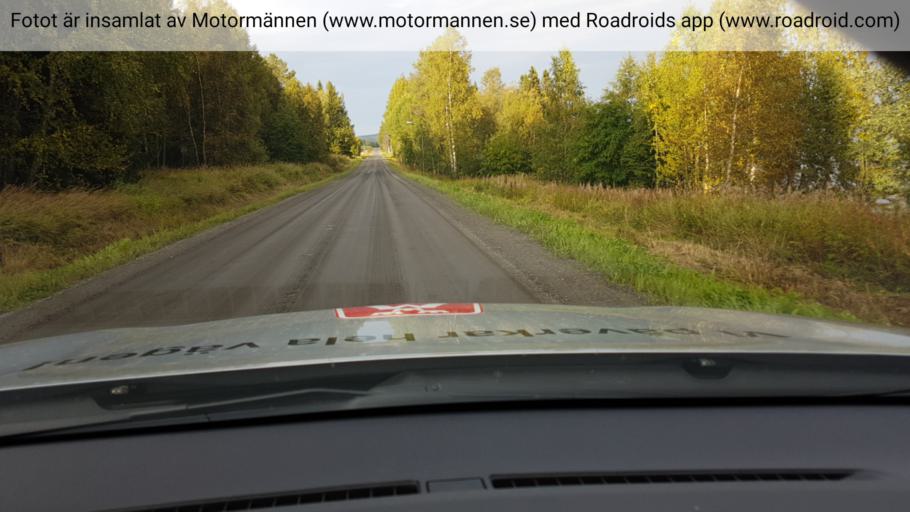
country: SE
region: Jaemtland
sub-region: Stroemsunds Kommun
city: Stroemsund
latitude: 64.0421
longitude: 15.8101
